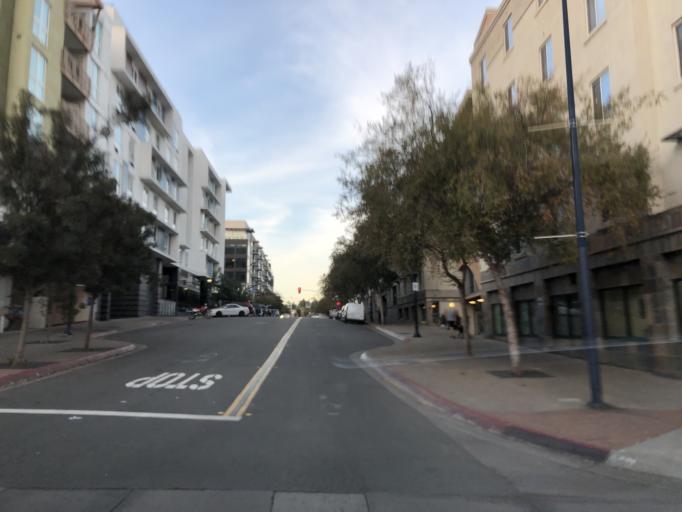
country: US
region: California
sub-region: San Diego County
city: San Diego
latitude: 32.7105
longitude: -117.1519
